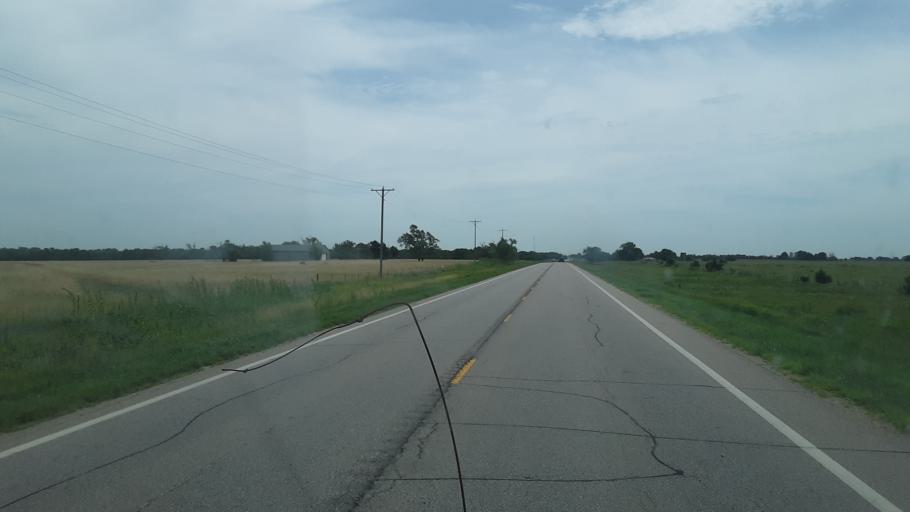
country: US
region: Kansas
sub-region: Butler County
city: El Dorado
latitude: 37.8106
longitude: -96.6404
